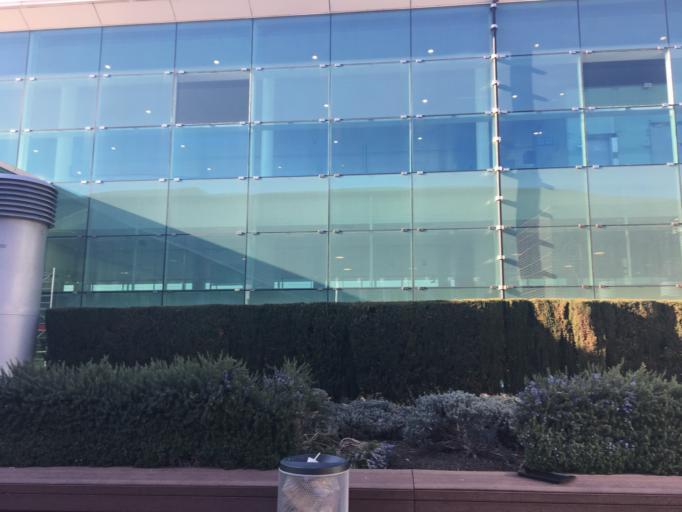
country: ES
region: Catalonia
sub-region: Provincia de Barcelona
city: El Prat de Llobregat
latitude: 41.2906
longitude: 2.0740
